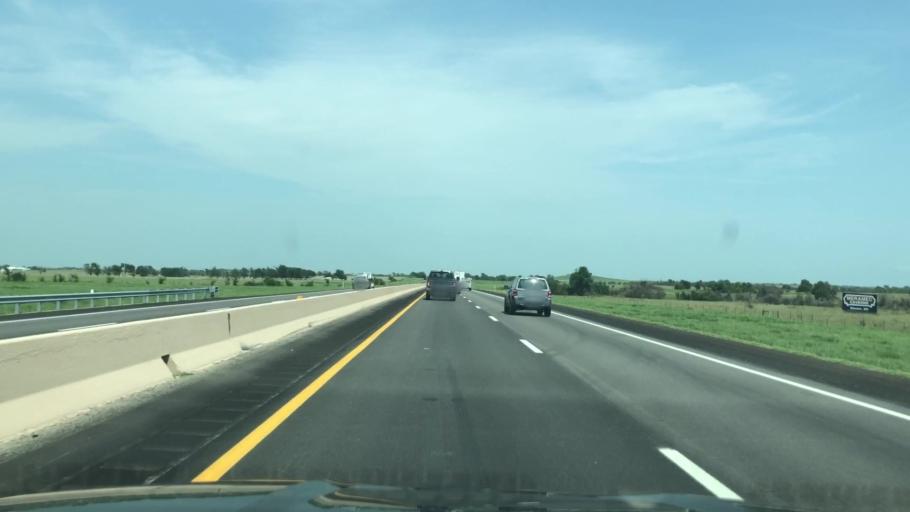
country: US
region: Oklahoma
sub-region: Ottawa County
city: Afton
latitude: 36.6765
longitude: -95.0533
